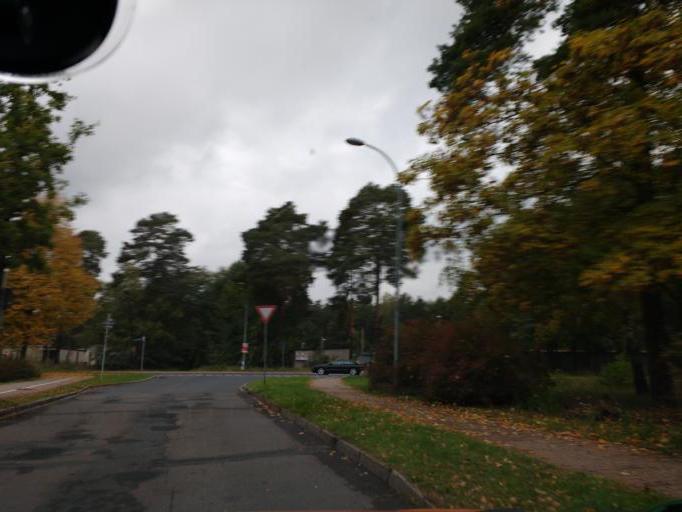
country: DE
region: Brandenburg
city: Ludwigsfelde
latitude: 52.3127
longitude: 13.2483
